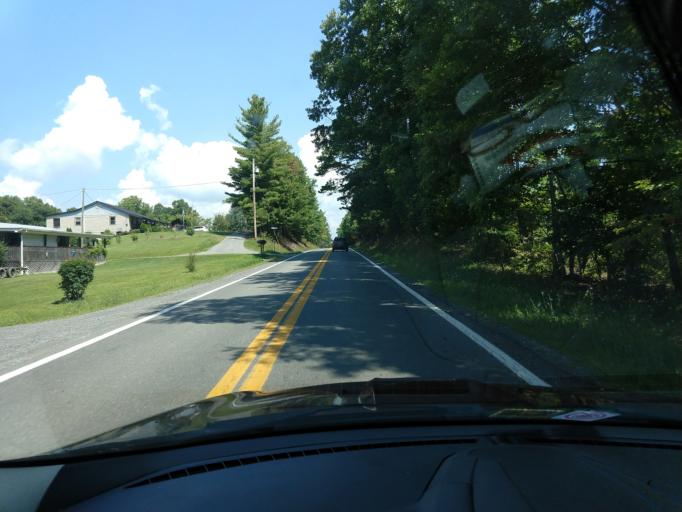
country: US
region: West Virginia
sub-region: Greenbrier County
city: Fairlea
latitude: 37.8362
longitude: -80.5552
